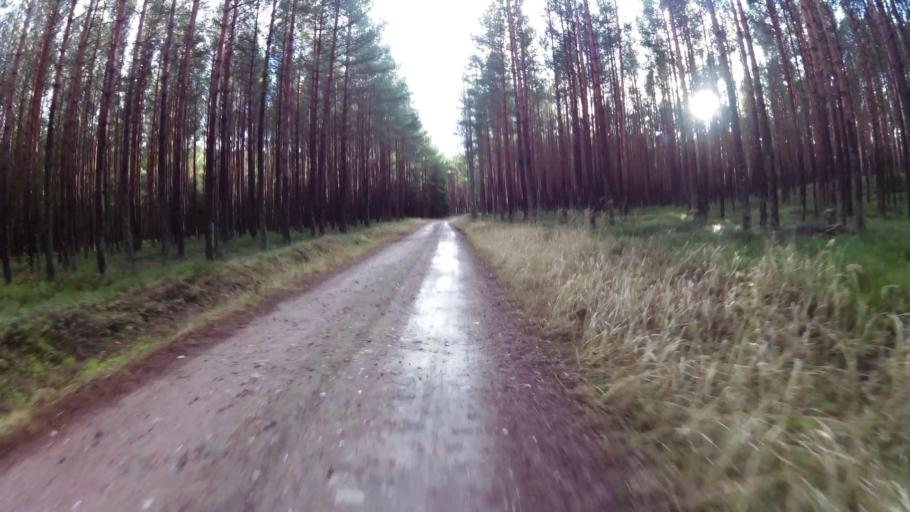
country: PL
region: West Pomeranian Voivodeship
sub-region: Powiat koszalinski
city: Sianow
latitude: 54.1038
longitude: 16.2982
